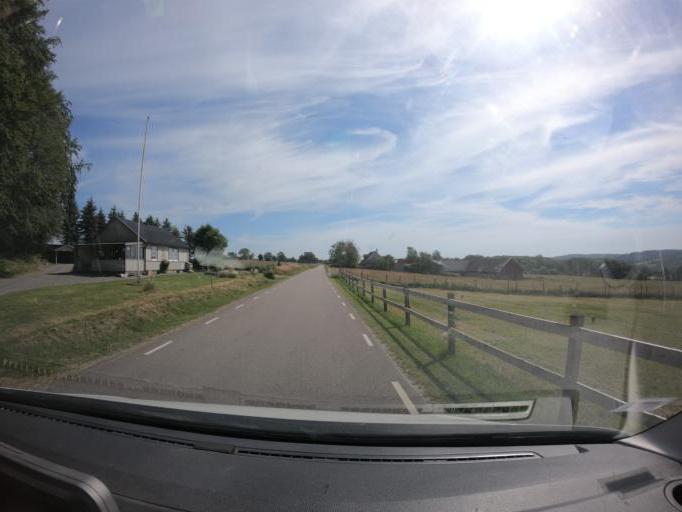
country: SE
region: Skane
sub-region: Bastads Kommun
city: Bastad
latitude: 56.4149
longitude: 12.7977
